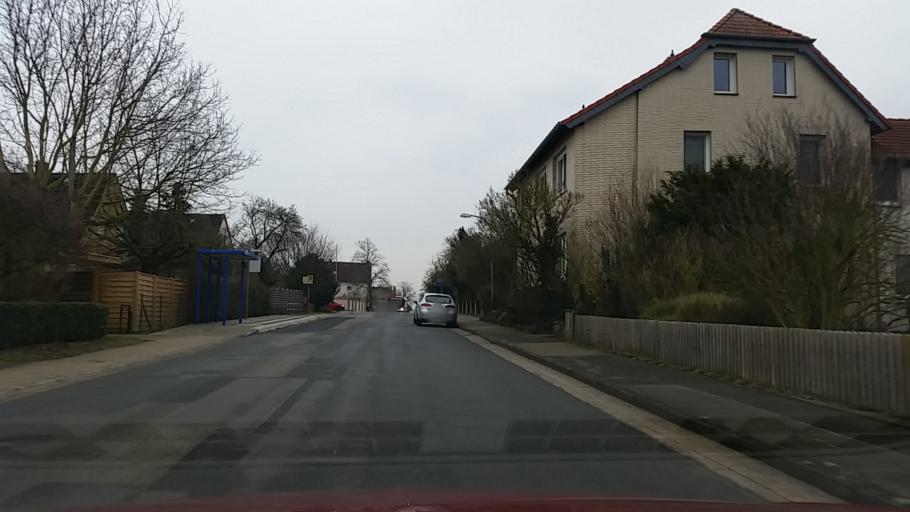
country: DE
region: Lower Saxony
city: Meine
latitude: 52.3561
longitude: 10.5878
